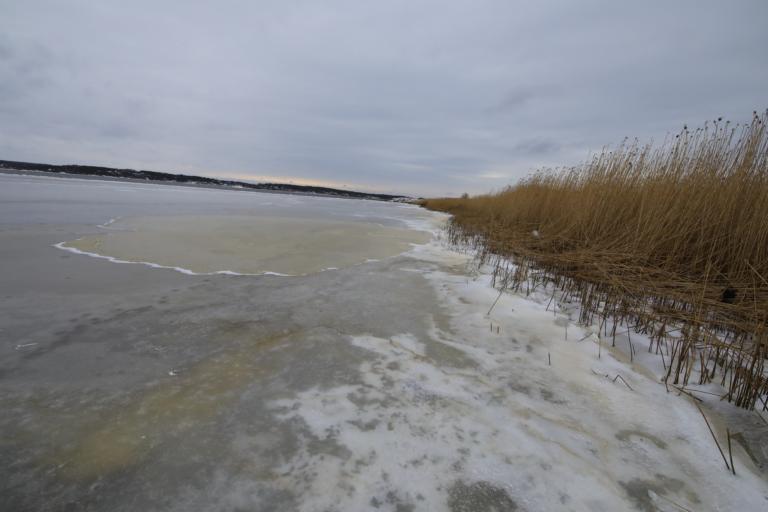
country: SE
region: Halland
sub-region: Kungsbacka Kommun
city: Frillesas
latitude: 57.2171
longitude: 12.1816
